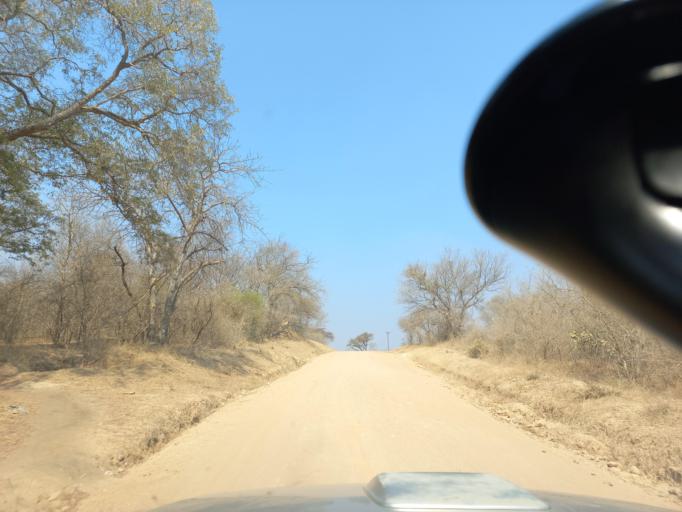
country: ZW
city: Chirundu
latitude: -15.9255
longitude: 28.8827
